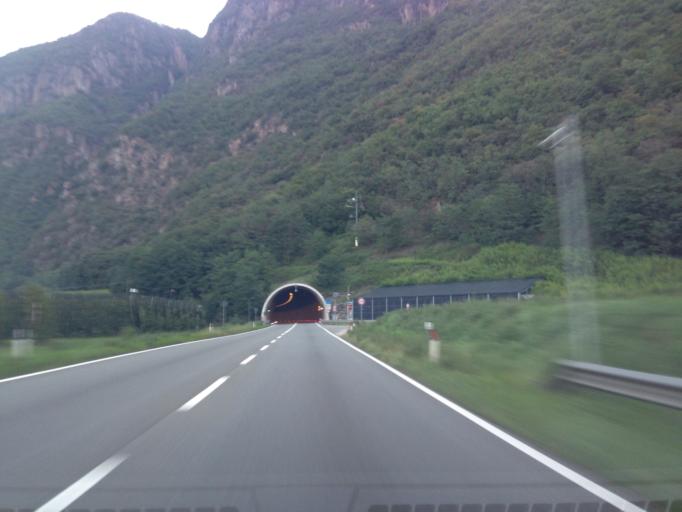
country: IT
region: Trentino-Alto Adige
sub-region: Bolzano
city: Pineta
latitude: 46.4486
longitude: 11.3443
